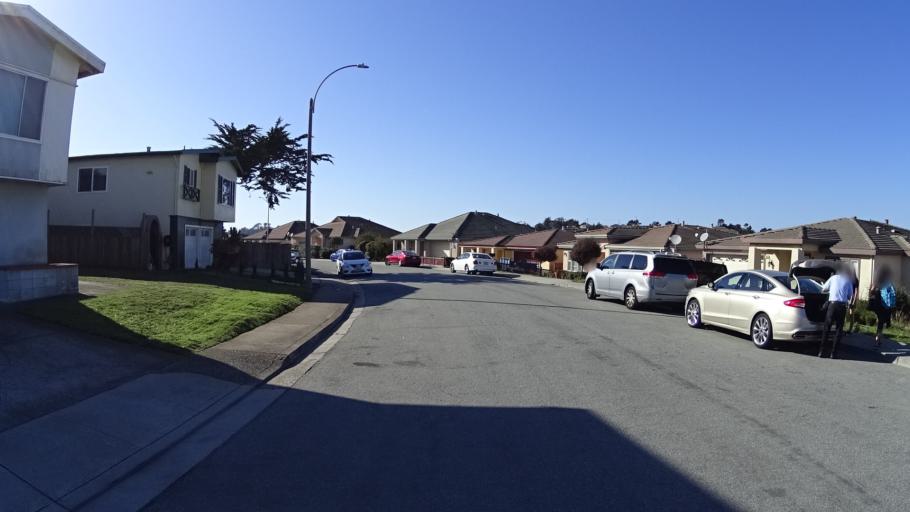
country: US
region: California
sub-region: San Mateo County
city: Pacifica
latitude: 37.6319
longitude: -122.4572
